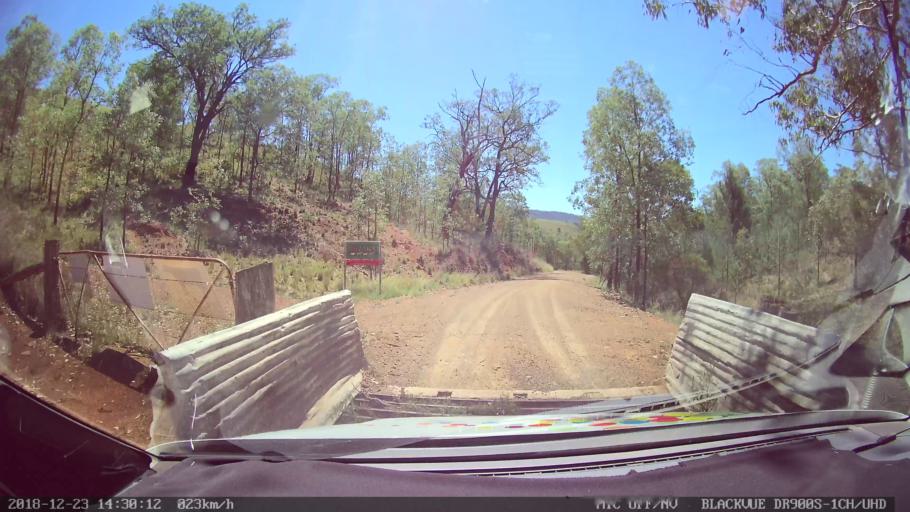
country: AU
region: New South Wales
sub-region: Tamworth Municipality
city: Manilla
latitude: -30.6047
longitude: 150.9335
